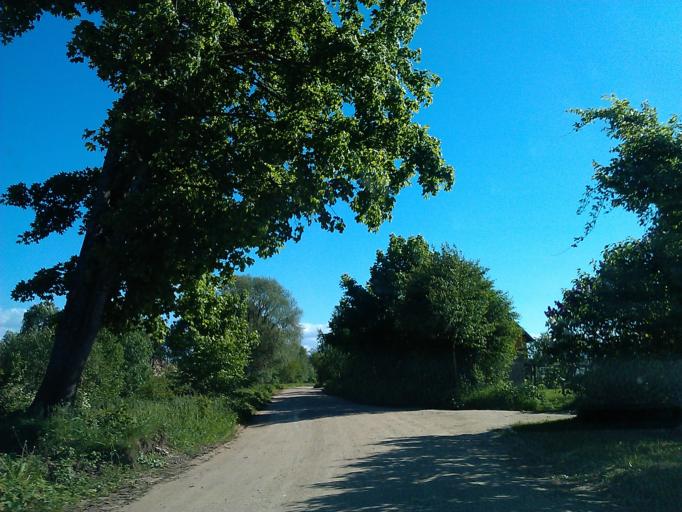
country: LV
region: Adazi
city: Adazi
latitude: 57.0912
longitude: 24.3222
